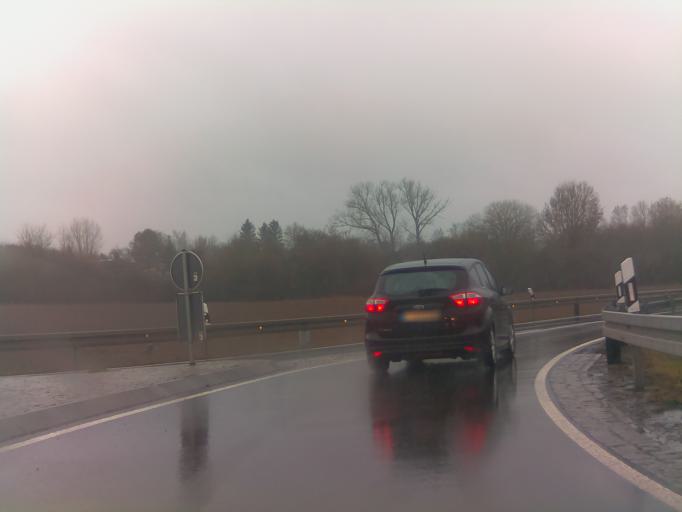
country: DE
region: Thuringia
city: Eisfeld
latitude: 50.4324
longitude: 10.8966
